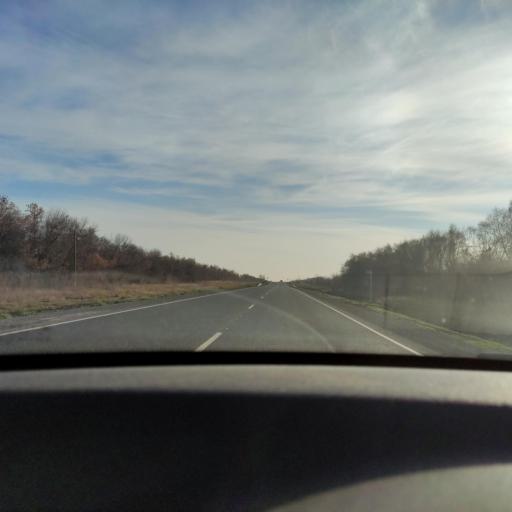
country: RU
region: Samara
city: Krasnoarmeyskoye
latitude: 52.8137
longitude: 50.0111
